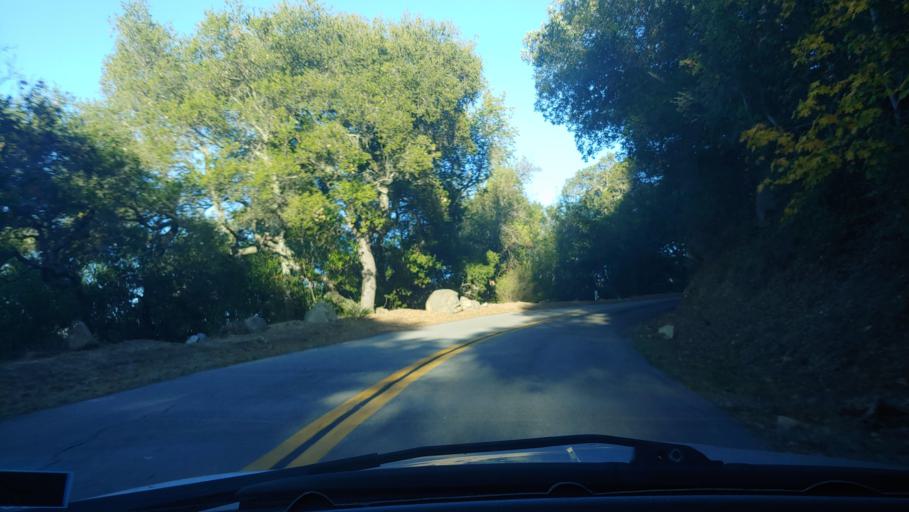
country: US
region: California
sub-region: Santa Barbara County
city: Goleta
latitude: 34.5148
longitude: -119.8305
